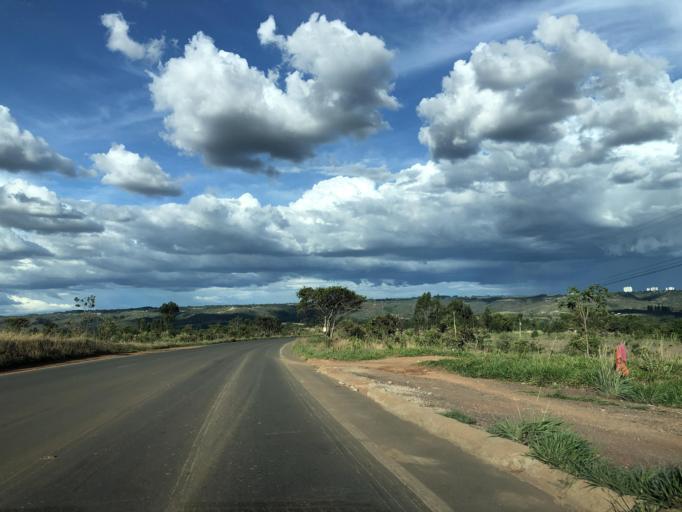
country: BR
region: Goias
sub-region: Luziania
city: Luziania
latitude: -16.0090
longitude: -48.1339
